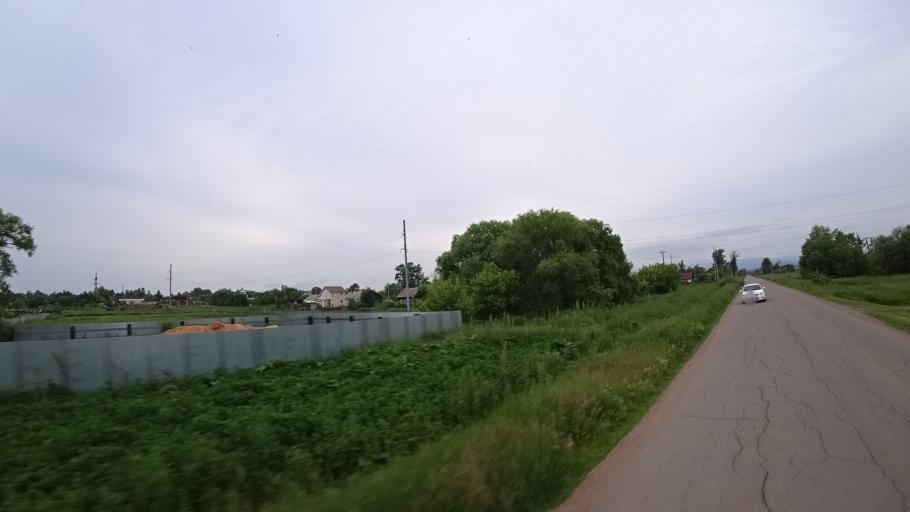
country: RU
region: Primorskiy
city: Novosysoyevka
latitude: 44.2331
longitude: 133.3708
